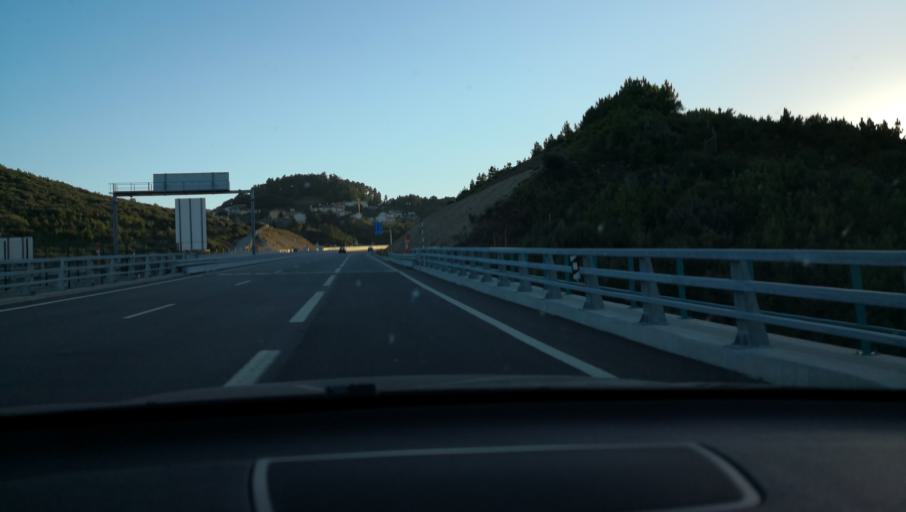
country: PT
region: Vila Real
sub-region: Vila Real
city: Vila Real
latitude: 41.2684
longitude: -7.7866
